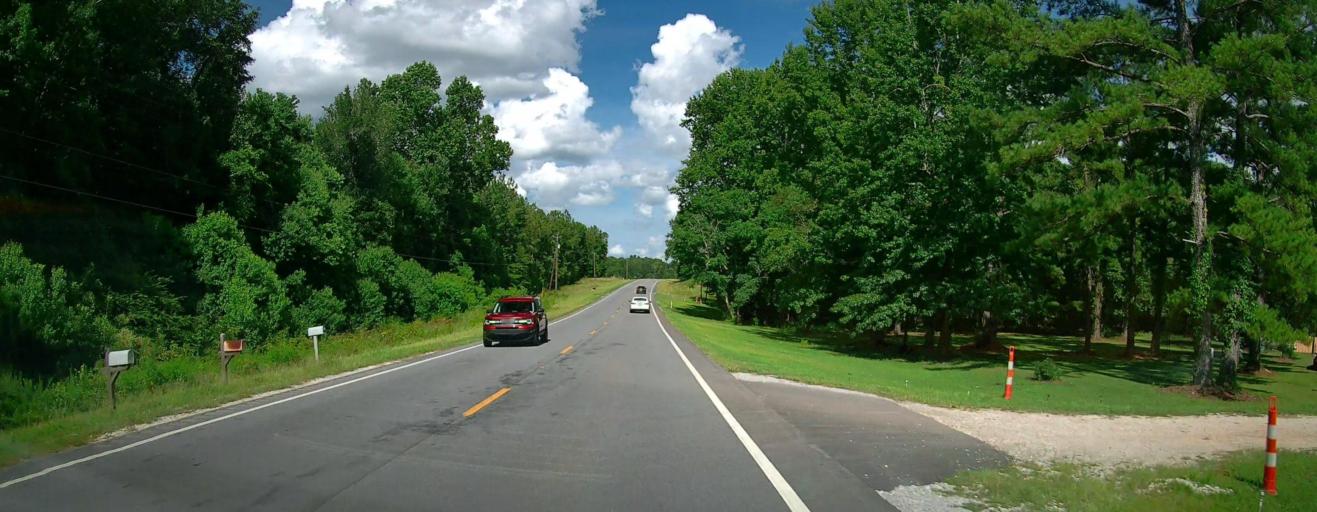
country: US
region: Alabama
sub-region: Lee County
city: Auburn
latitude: 32.4385
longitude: -85.3778
